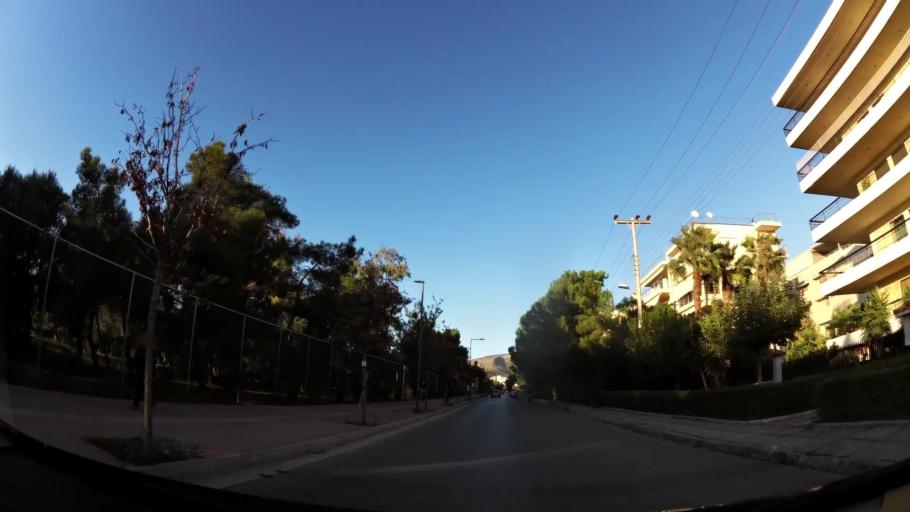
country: GR
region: Attica
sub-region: Nomarchia Athinas
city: Glyfada
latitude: 37.8729
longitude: 23.7502
